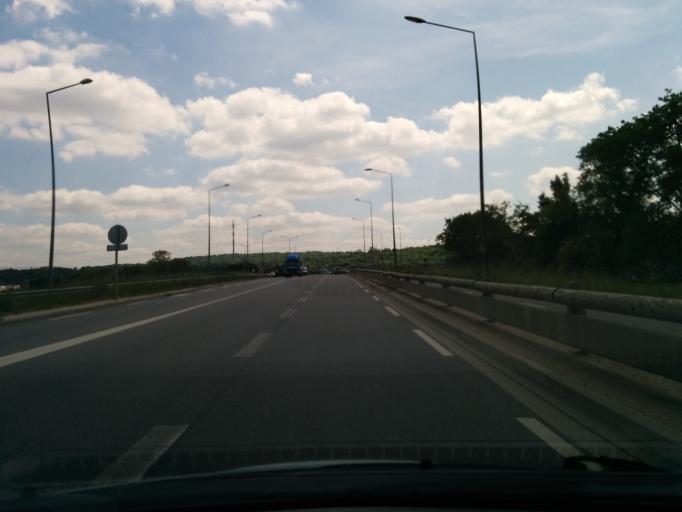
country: FR
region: Ile-de-France
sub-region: Departement des Yvelines
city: Flins-sur-Seine
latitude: 48.9719
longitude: 1.8635
